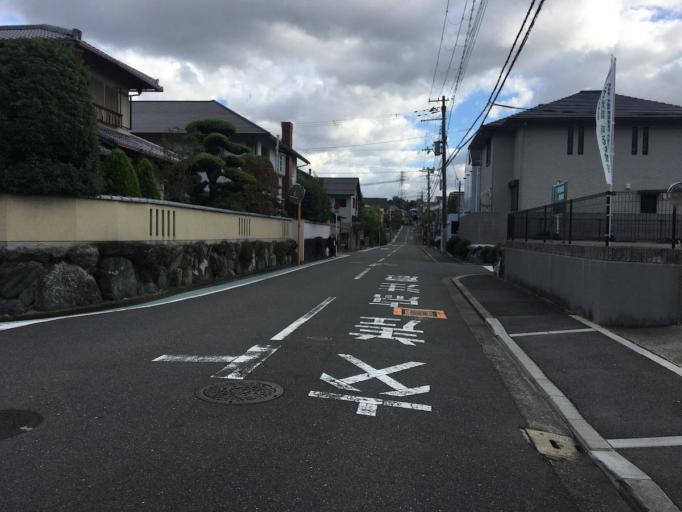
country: JP
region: Osaka
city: Suita
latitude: 34.8025
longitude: 135.5160
